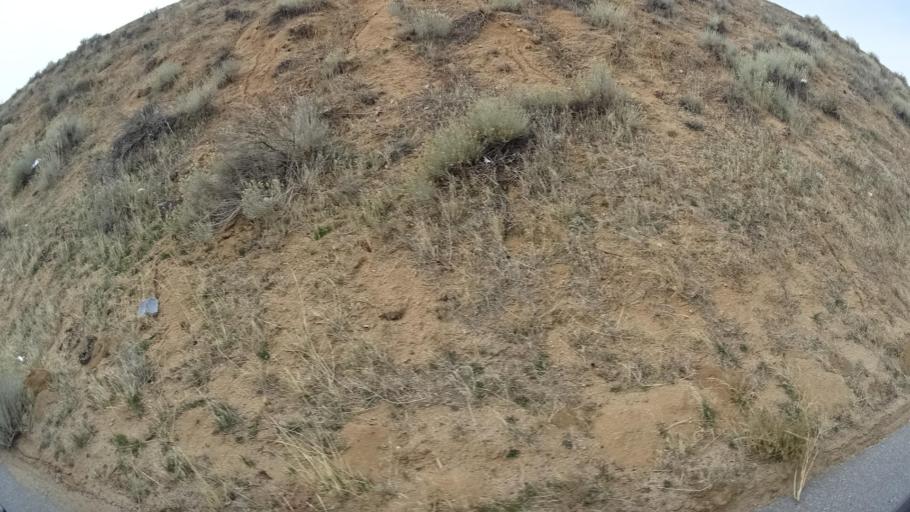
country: US
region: California
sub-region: Kern County
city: Tehachapi
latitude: 35.0843
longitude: -118.3951
